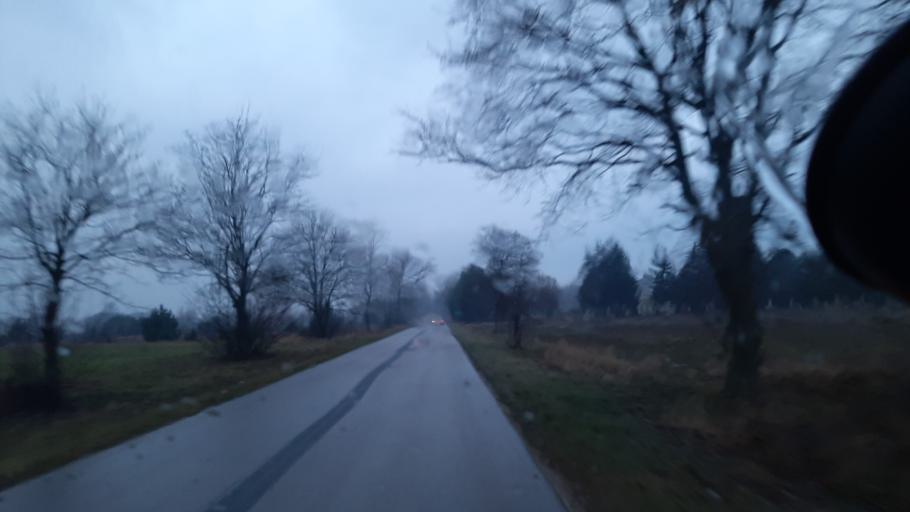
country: PL
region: Lublin Voivodeship
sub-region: Powiat lubartowski
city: Firlej
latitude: 51.5569
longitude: 22.5349
